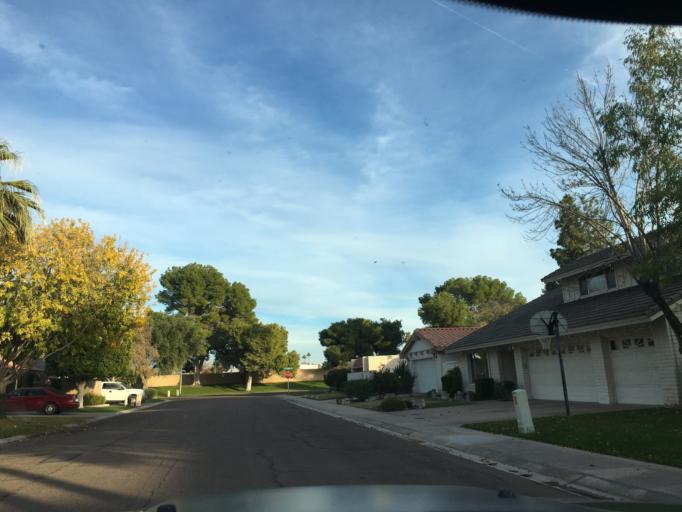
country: US
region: Arizona
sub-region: Maricopa County
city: Tempe
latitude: 33.3761
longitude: -111.9123
